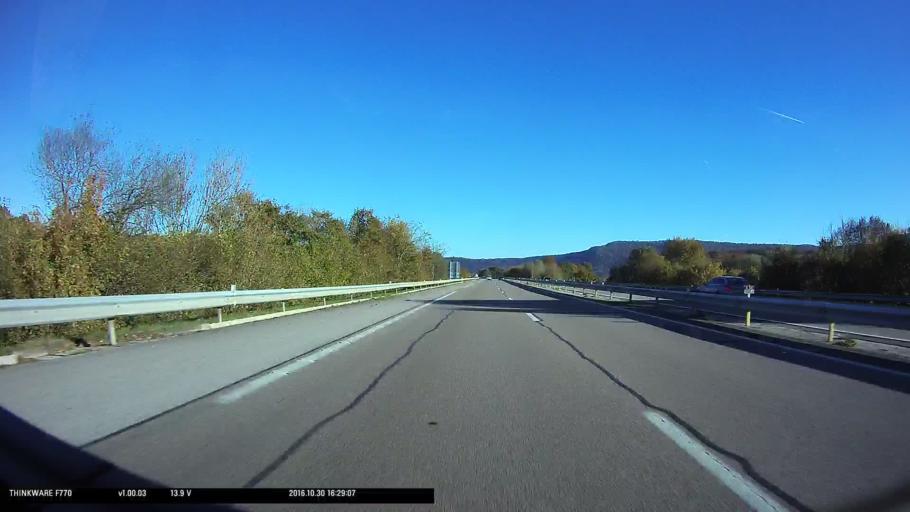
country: FR
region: Franche-Comte
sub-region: Departement du Doubs
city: Roulans
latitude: 47.3422
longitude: 6.2735
